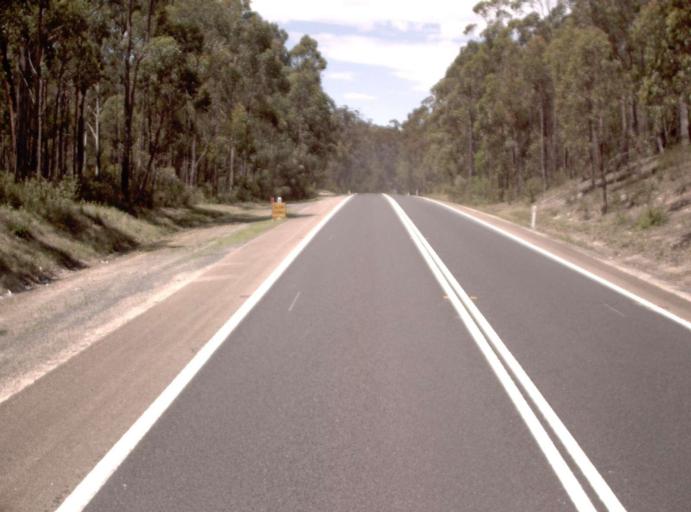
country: AU
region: New South Wales
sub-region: Bombala
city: Bombala
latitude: -37.5663
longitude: 149.0993
